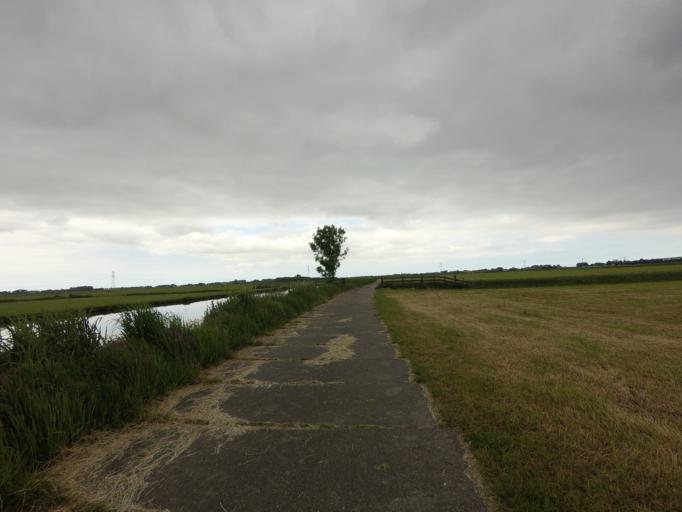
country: NL
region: North Holland
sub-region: Gemeente Hoorn
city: Hoorn
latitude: 52.6573
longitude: 5.0236
